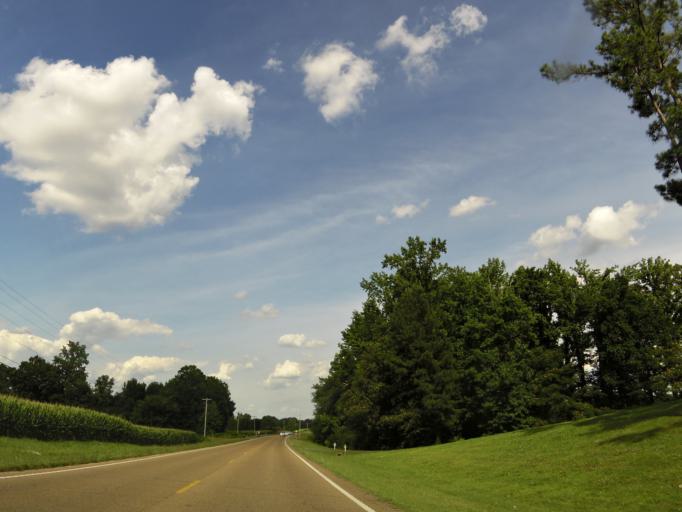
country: US
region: Tennessee
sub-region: Carroll County
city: Bruceton
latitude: 36.0377
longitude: -88.3109
